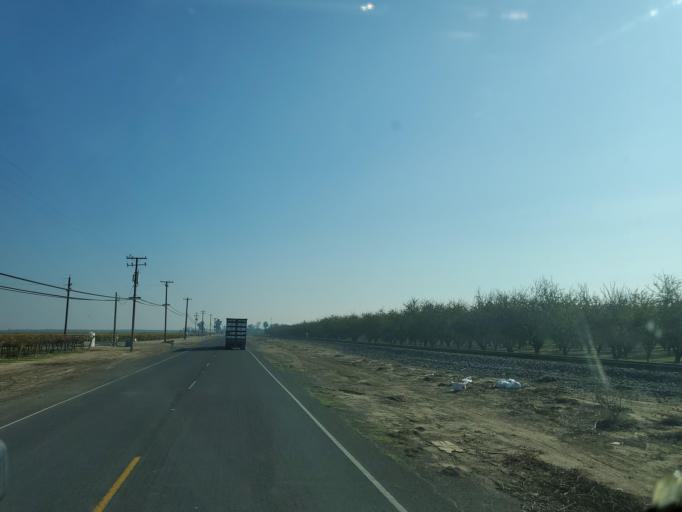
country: US
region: California
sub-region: San Joaquin County
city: Manteca
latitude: 37.8569
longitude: -121.2094
